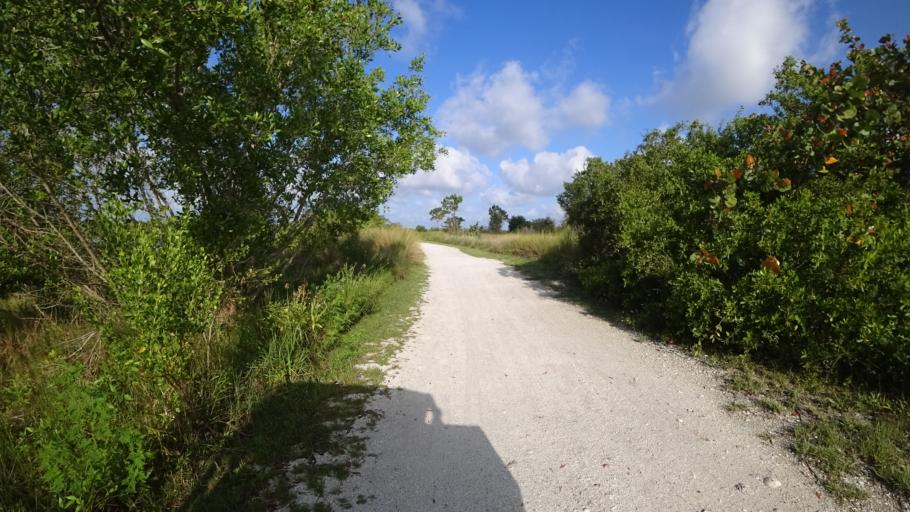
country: US
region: Florida
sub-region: Manatee County
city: West Bradenton
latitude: 27.5162
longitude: -82.6637
